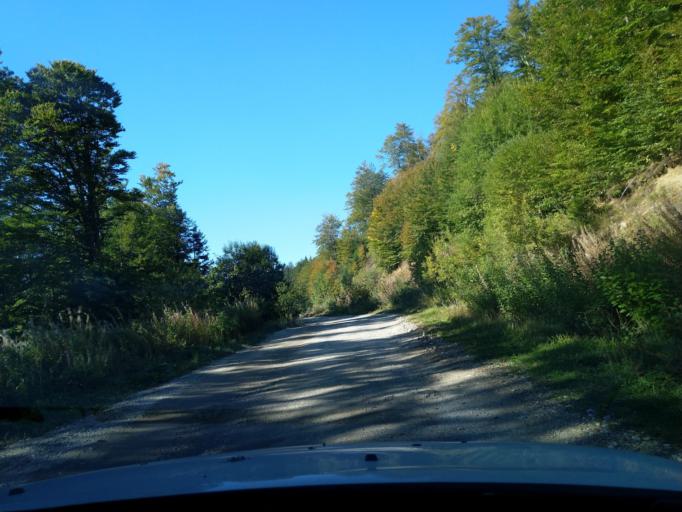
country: RS
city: Sokolovica
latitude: 43.3673
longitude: 20.2591
